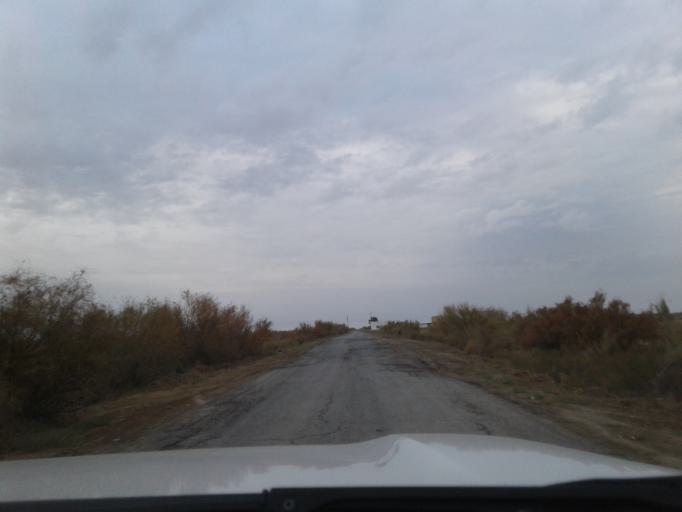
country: TM
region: Mary
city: Mary
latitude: 38.4380
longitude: 61.6685
